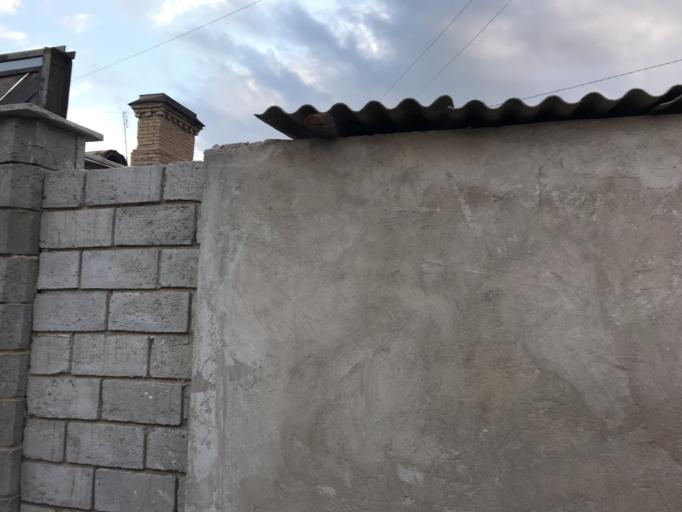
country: UZ
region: Bukhara
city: Kogon
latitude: 39.7188
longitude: 64.5477
